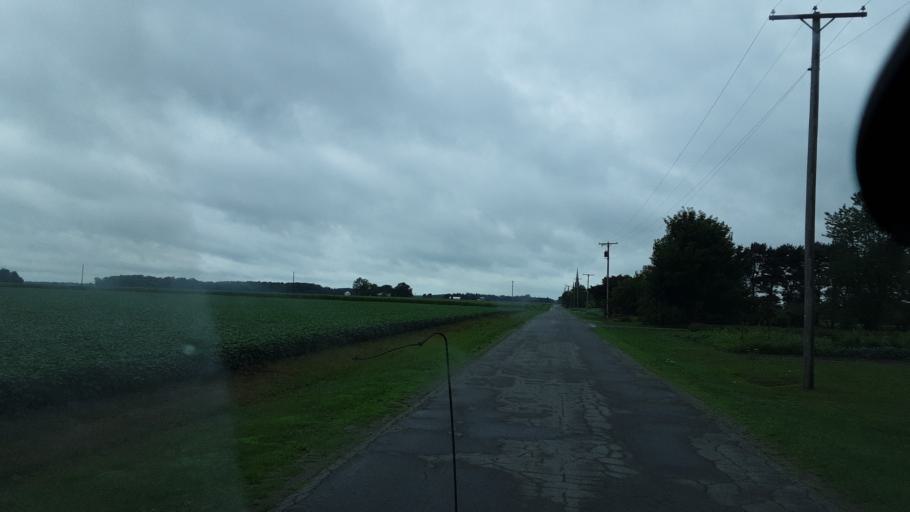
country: US
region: Ohio
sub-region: Van Wert County
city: Convoy
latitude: 40.8223
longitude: -84.6954
